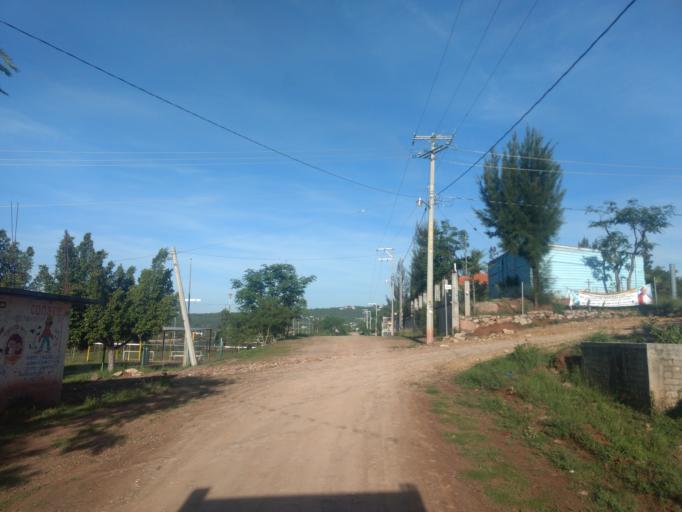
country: MX
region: Oaxaca
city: Ciudad de Huajuapam de Leon
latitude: 17.8259
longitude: -97.7914
